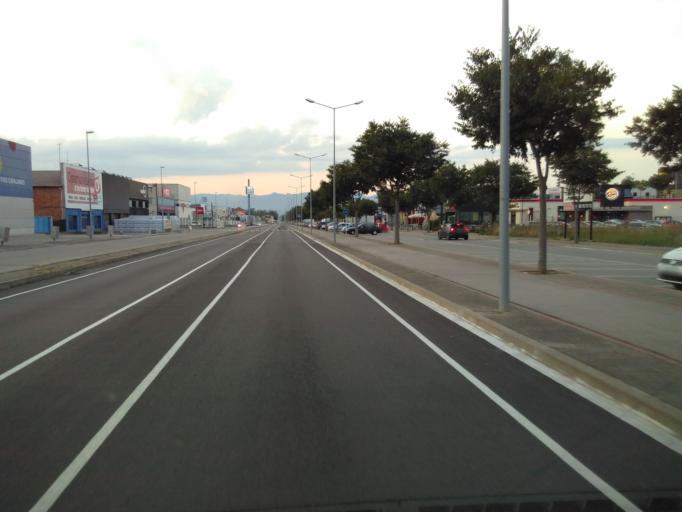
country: ES
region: Catalonia
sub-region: Provincia de Barcelona
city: Vic
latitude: 41.9412
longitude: 2.2564
